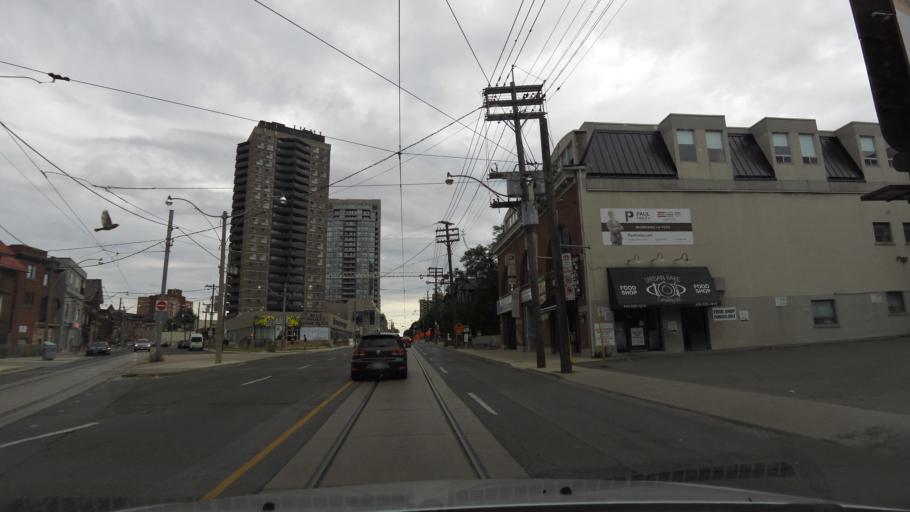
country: CA
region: Ontario
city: Toronto
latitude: 43.6812
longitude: -79.4174
